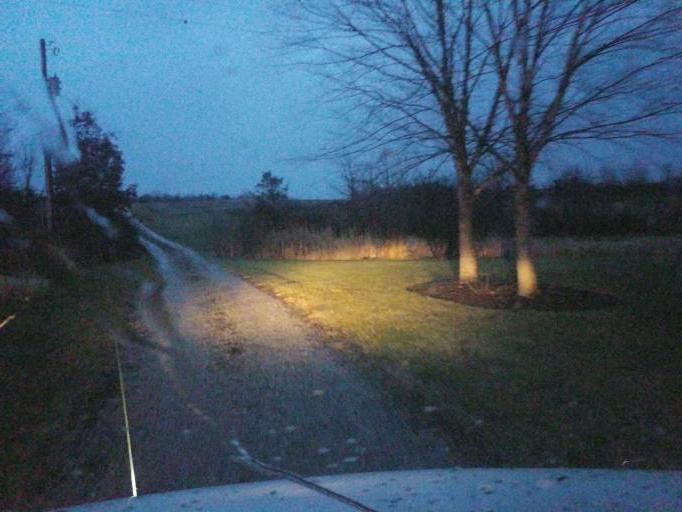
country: US
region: Ohio
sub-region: Knox County
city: Gambier
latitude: 40.3177
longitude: -82.4490
